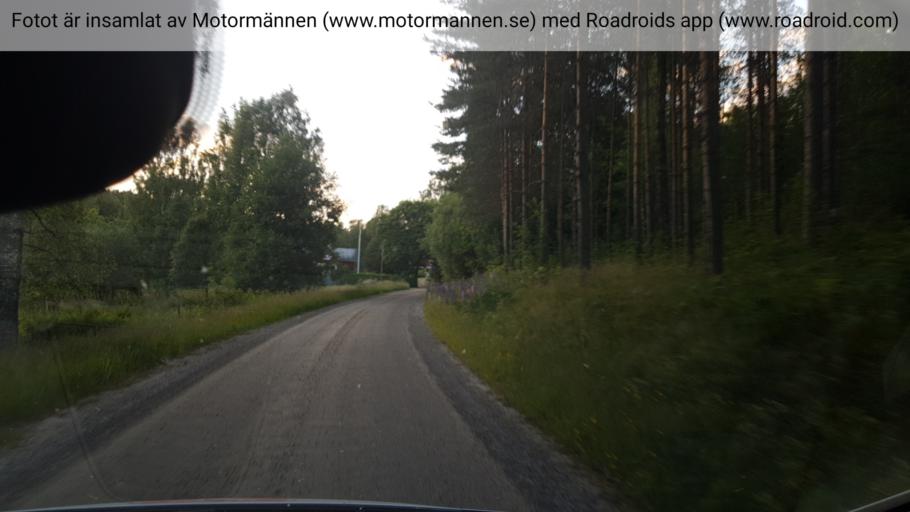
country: SE
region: Vaermland
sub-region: Sunne Kommun
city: Sunne
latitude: 59.7034
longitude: 12.8854
